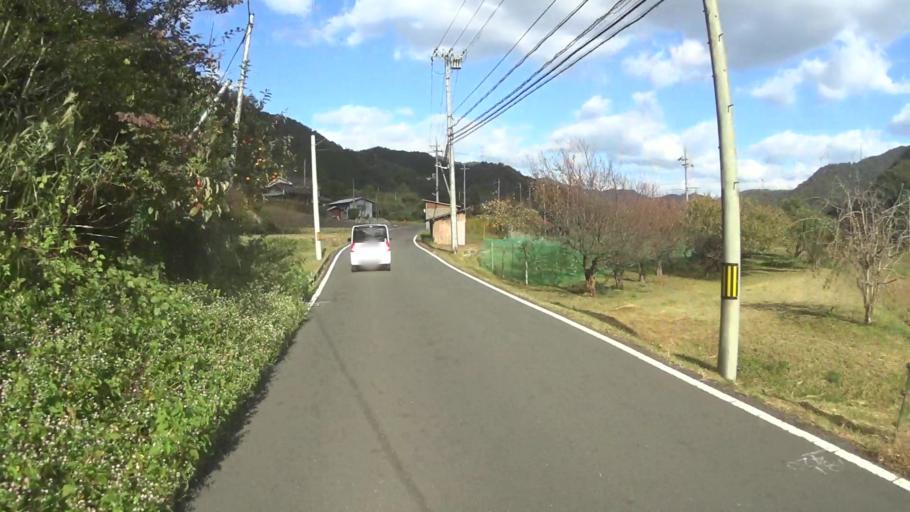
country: JP
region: Kyoto
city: Maizuru
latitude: 35.5231
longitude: 135.4069
